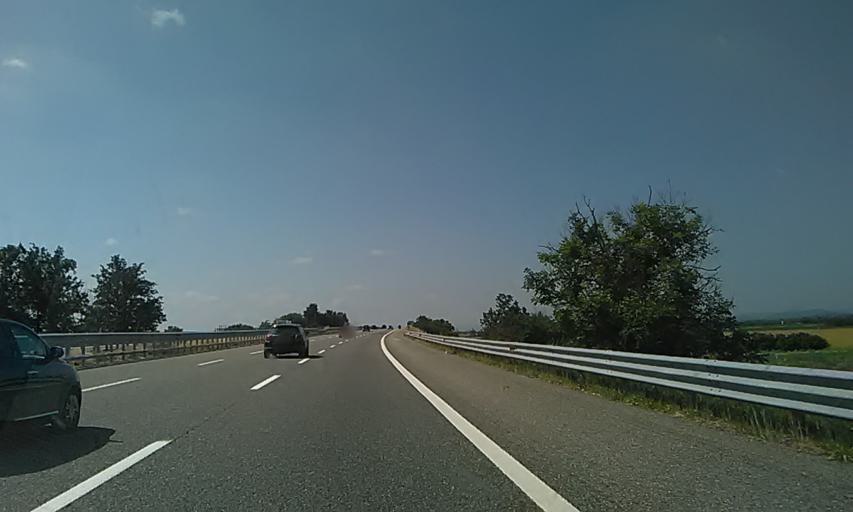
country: IT
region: Piedmont
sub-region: Provincia di Alessandria
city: Castellazzo Bormida
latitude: 44.8370
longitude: 8.5962
